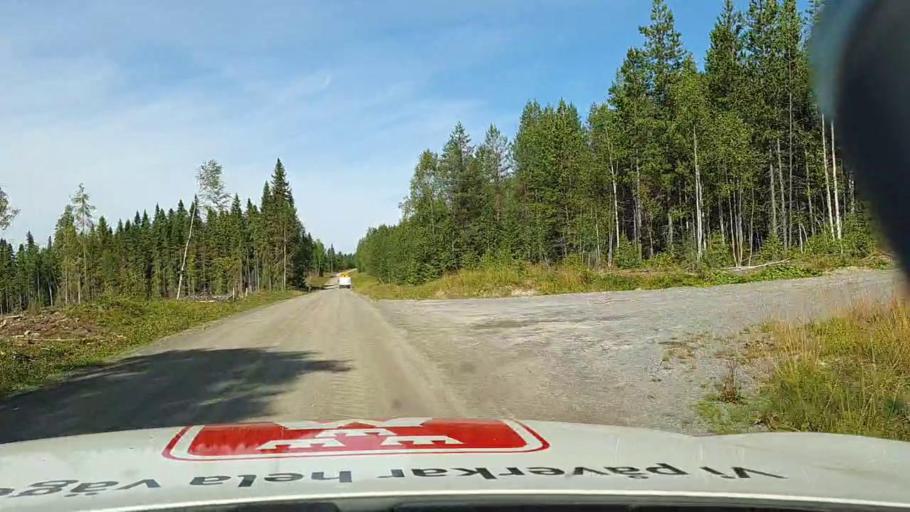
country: SE
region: Jaemtland
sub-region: Stroemsunds Kommun
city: Stroemsund
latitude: 63.7347
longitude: 15.2437
